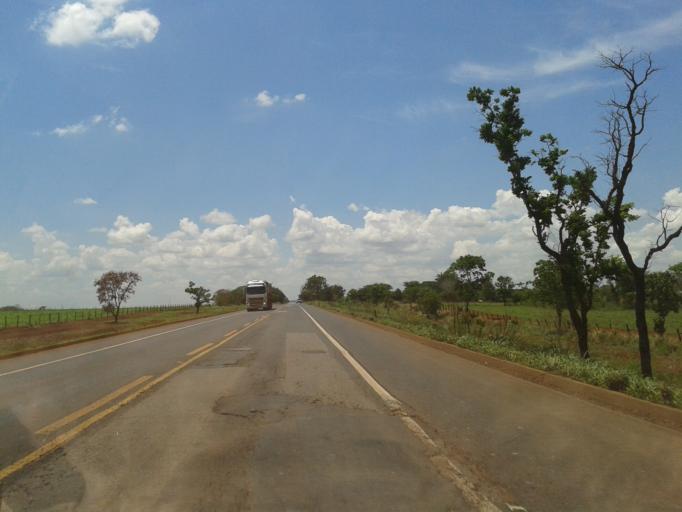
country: BR
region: Goias
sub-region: Goiatuba
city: Goiatuba
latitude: -18.2855
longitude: -49.6120
